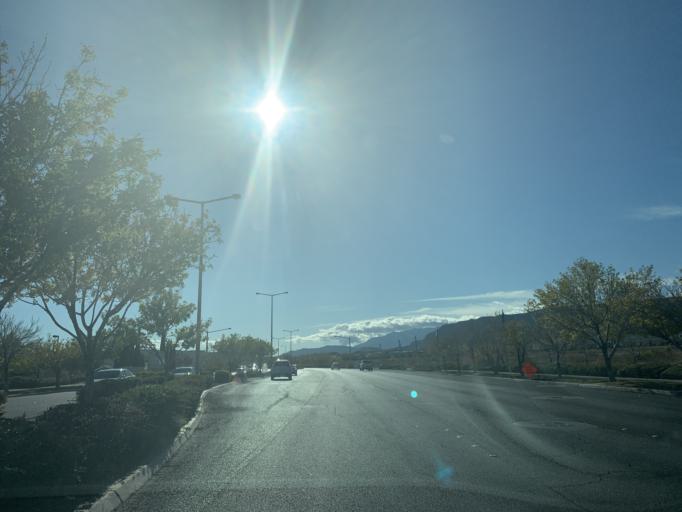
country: US
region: Nevada
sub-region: Clark County
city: Summerlin South
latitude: 36.1204
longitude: -115.3276
